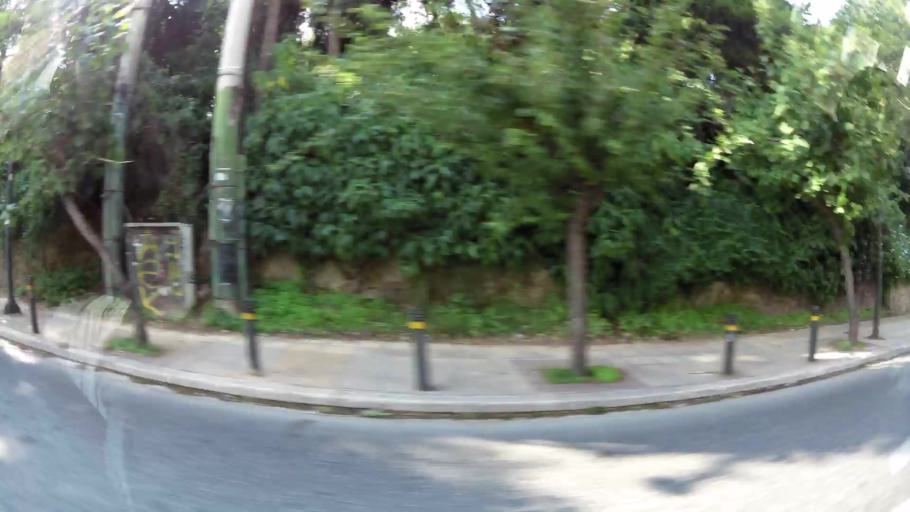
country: GR
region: Attica
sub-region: Nomarchia Athinas
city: Dhafni
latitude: 37.9628
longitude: 23.7338
